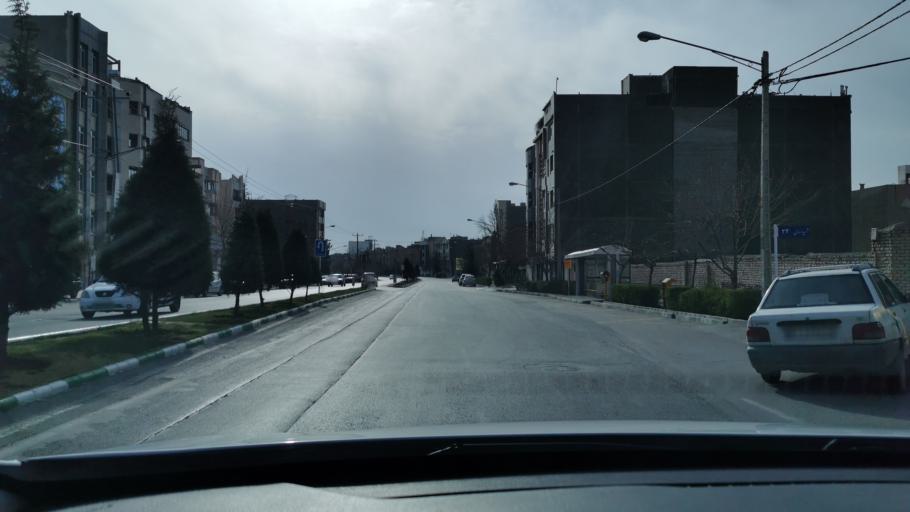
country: IR
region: Razavi Khorasan
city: Mashhad
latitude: 36.3152
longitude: 59.5101
